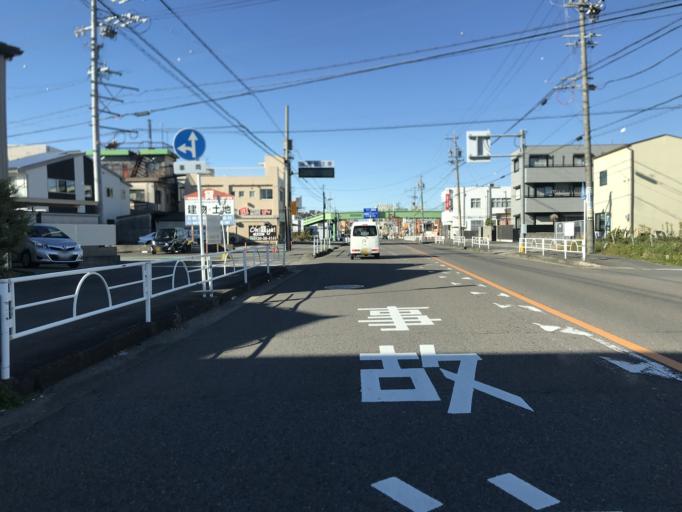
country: JP
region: Aichi
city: Nagoya-shi
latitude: 35.1973
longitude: 136.8647
